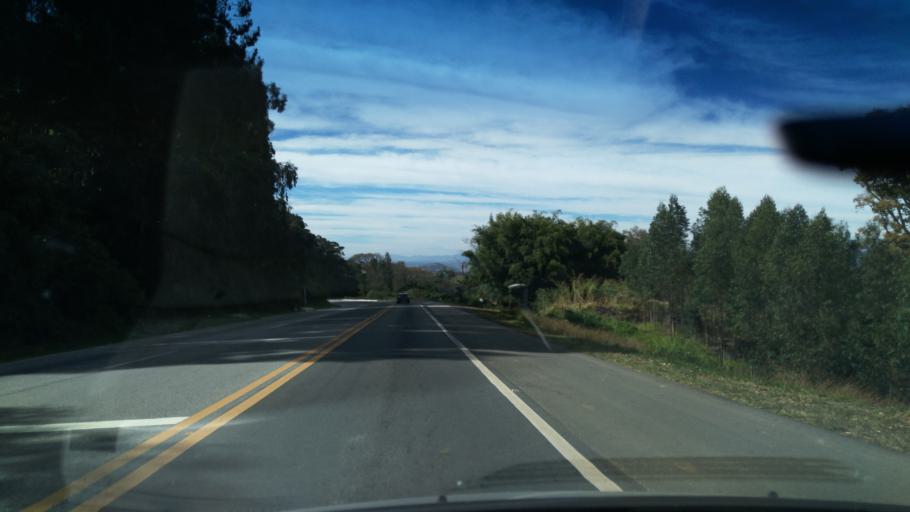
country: BR
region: Minas Gerais
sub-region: Borda Da Mata
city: Borda da Mata
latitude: -22.1345
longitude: -46.1748
